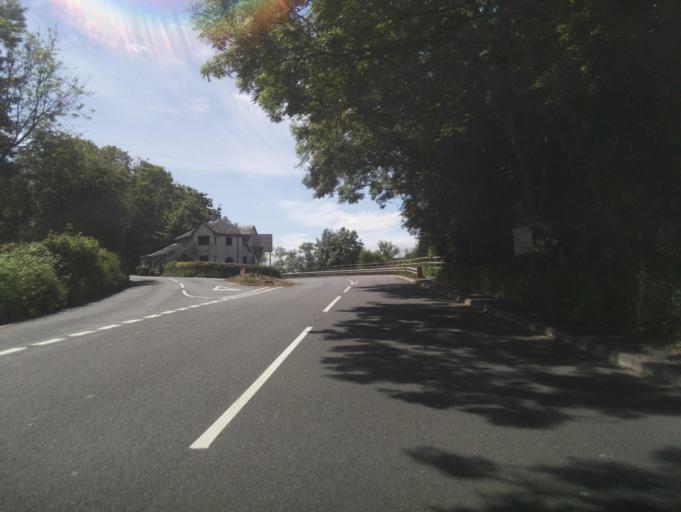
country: GB
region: Wales
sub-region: Monmouthshire
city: Monmouth
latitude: 51.8004
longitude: -2.7184
